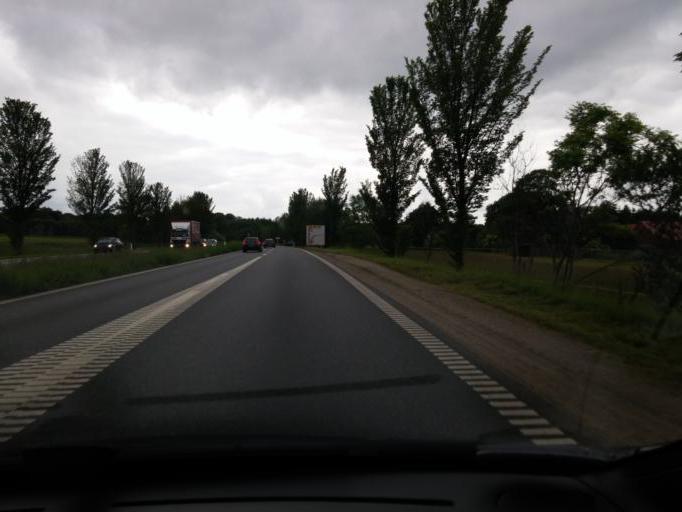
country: DK
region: Capital Region
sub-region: Hillerod Kommune
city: Hillerod
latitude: 55.9521
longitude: 12.3175
